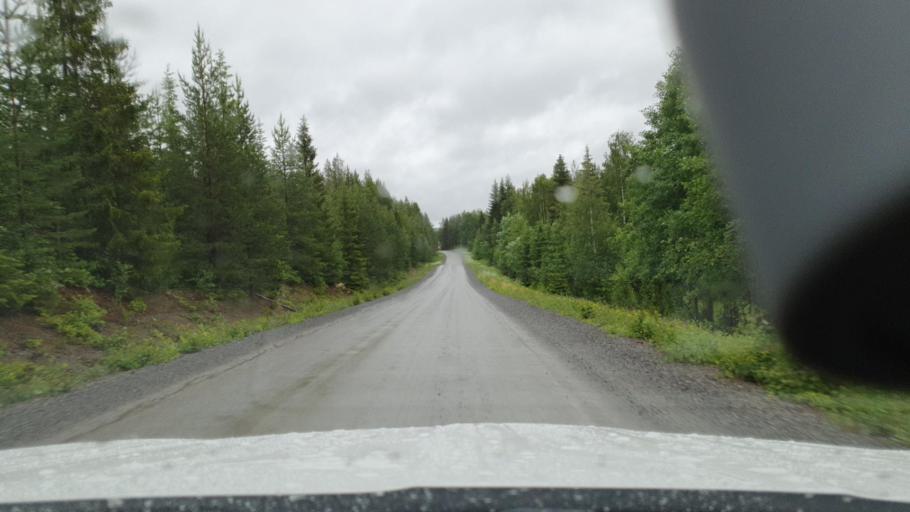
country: SE
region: Vaesterbotten
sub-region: Skelleftea Kommun
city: Burtraesk
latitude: 64.3710
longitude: 20.3780
